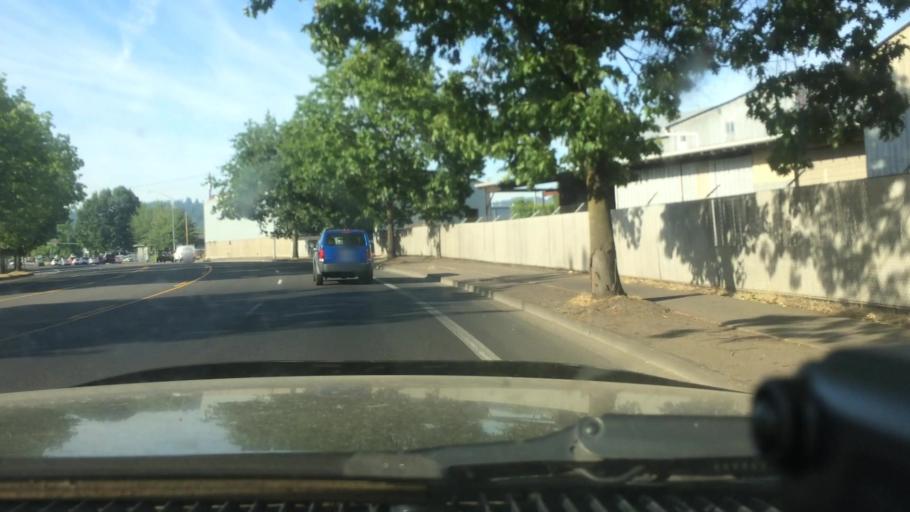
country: US
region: Oregon
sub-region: Lane County
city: Eugene
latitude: 44.0557
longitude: -123.1185
